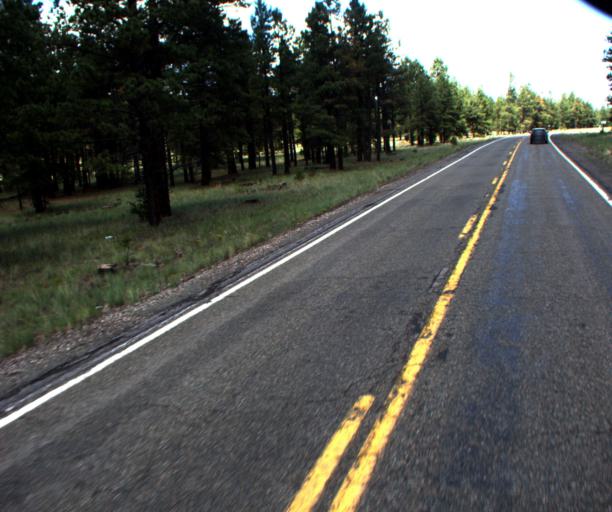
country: US
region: Arizona
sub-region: Coconino County
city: Parks
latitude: 35.3627
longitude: -111.7913
